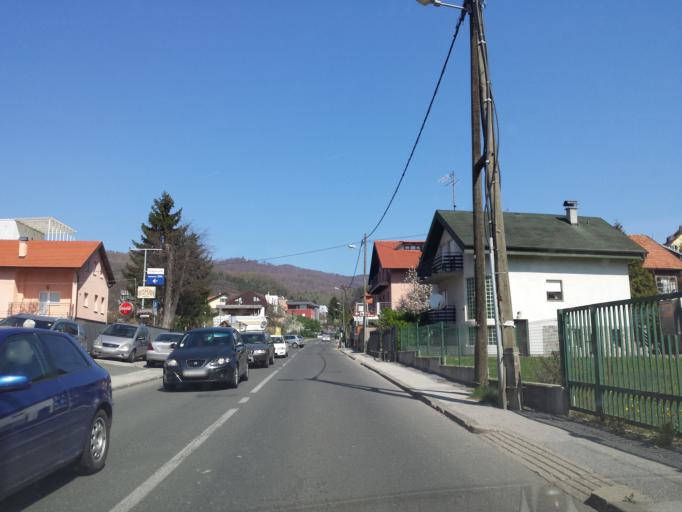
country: HR
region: Grad Zagreb
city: Zagreb
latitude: 45.8541
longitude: 15.9747
